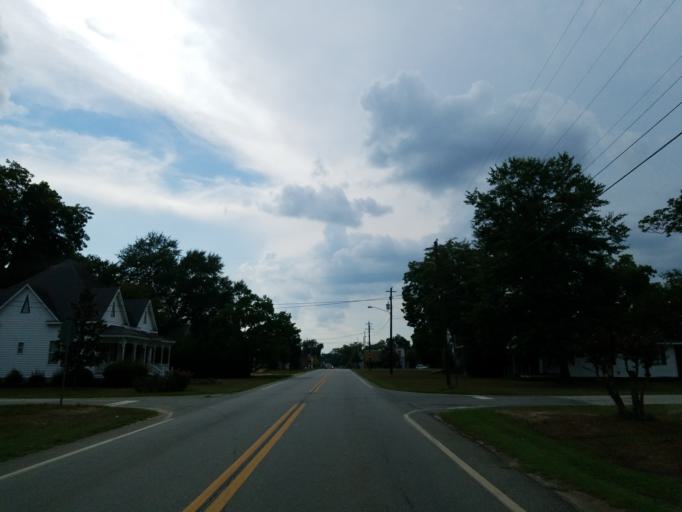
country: US
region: Georgia
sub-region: Dooly County
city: Unadilla
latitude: 32.2608
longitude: -83.7336
